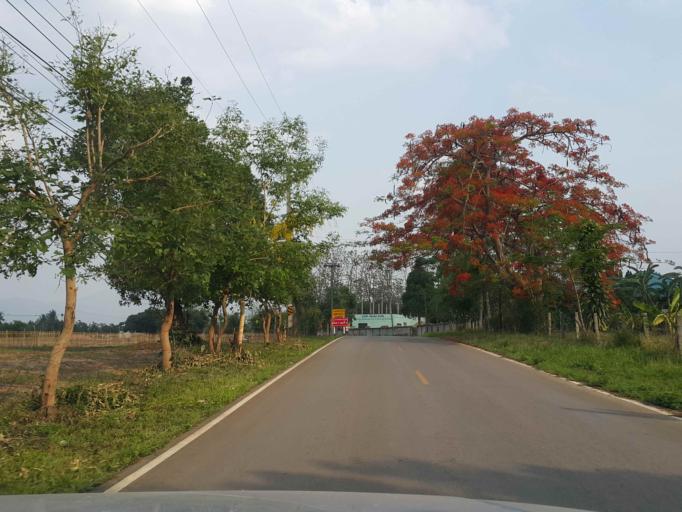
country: TH
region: Chiang Mai
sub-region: Amphoe Chiang Dao
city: Chiang Dao
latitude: 19.3791
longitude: 98.9438
